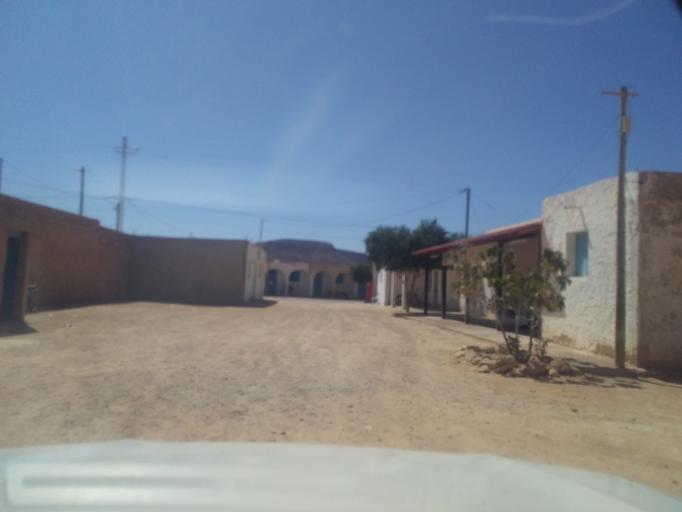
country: TN
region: Qabis
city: Matmata
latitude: 33.5144
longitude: 10.2181
